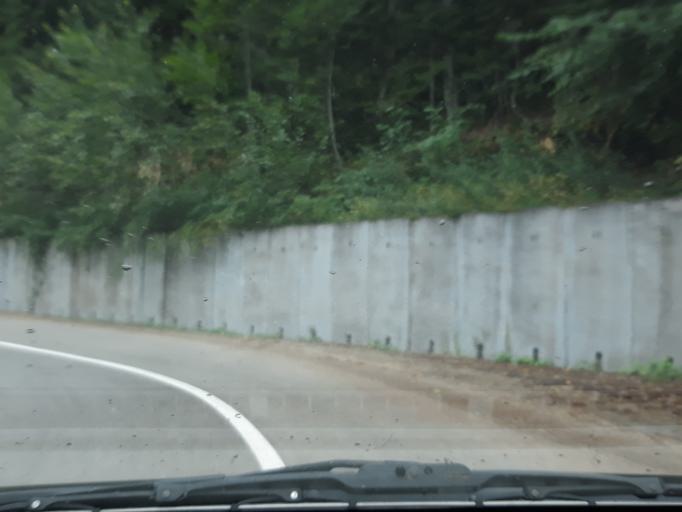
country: RO
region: Bihor
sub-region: Comuna Pietroasa
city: Pietroasa
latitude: 46.5960
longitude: 22.6729
